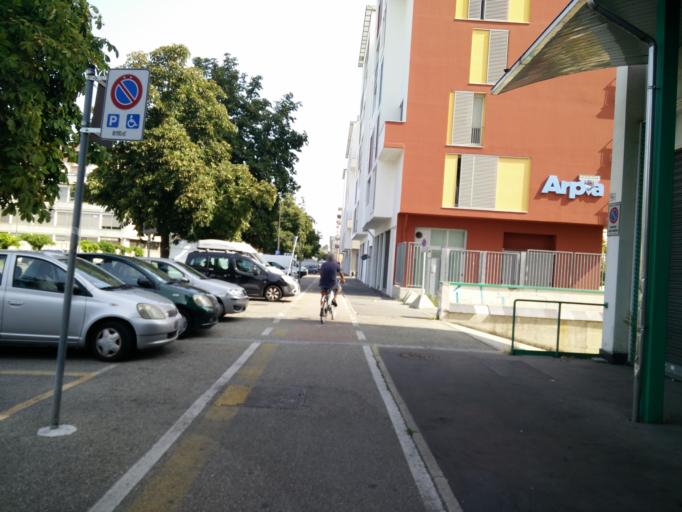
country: IT
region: Piedmont
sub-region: Provincia di Torino
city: Nichelino
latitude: 45.0286
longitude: 7.6544
